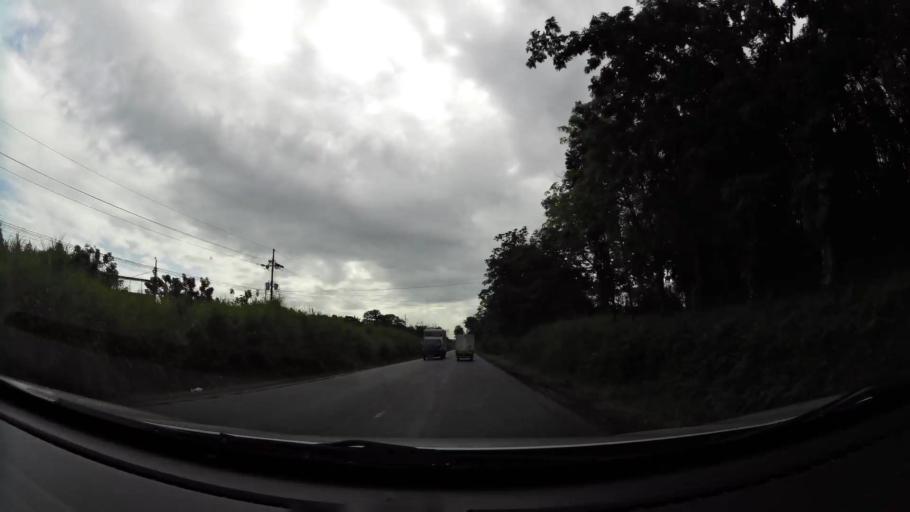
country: CR
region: Limon
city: Pocora
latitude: 10.1482
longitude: -83.5816
